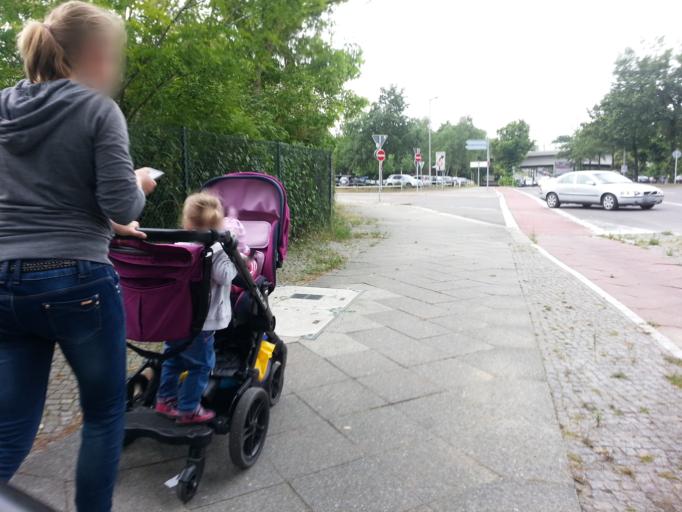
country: DE
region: Berlin
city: Charlottenburg-Nord
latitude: 52.5478
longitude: 13.3029
